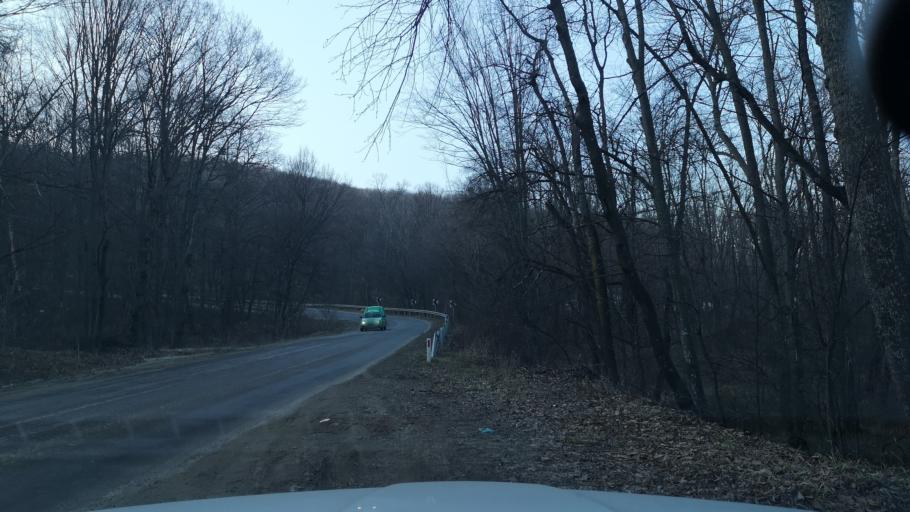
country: MD
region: Stinga Nistrului
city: Bucovat
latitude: 47.1392
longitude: 28.4978
